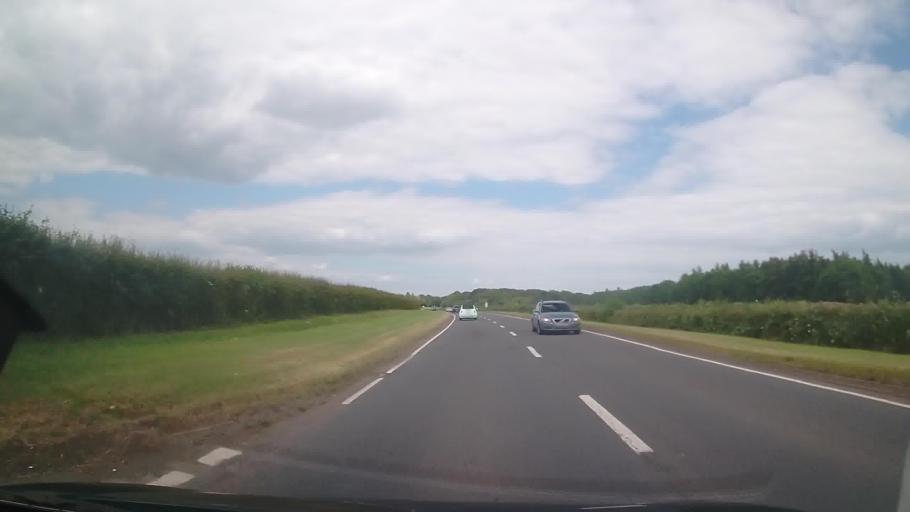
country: GB
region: England
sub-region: Herefordshire
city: Belmont
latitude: 52.0322
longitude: -2.7661
